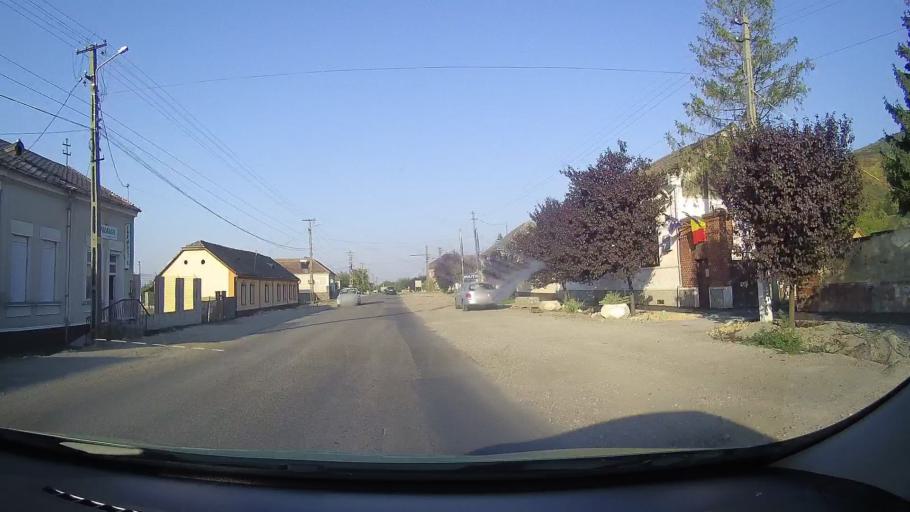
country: RO
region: Arad
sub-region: Comuna Siria
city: Siria
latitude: 46.2729
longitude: 21.6401
